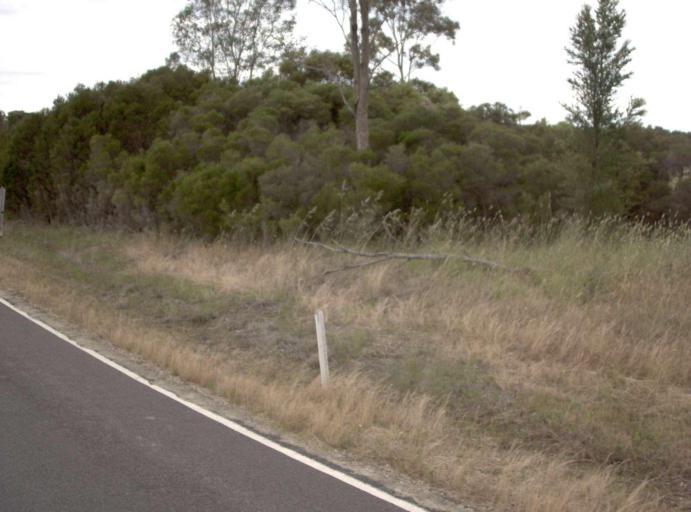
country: AU
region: Victoria
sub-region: East Gippsland
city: Bairnsdale
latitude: -37.9841
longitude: 147.4024
